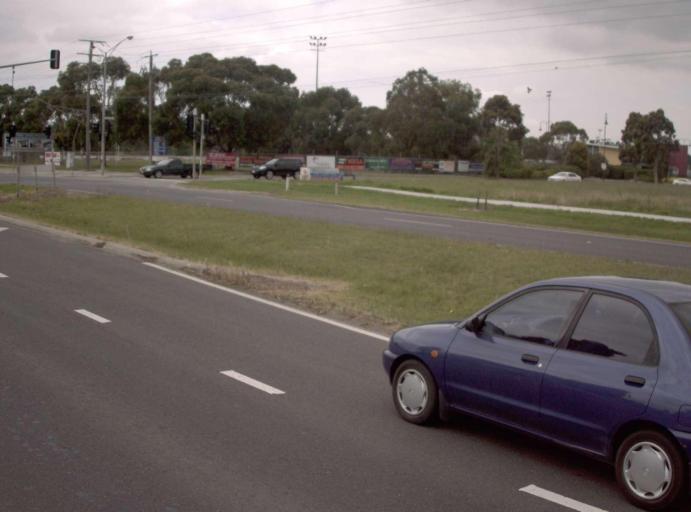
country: AU
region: Victoria
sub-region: Cardinia
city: Officer
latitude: -38.0628
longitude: 145.4596
